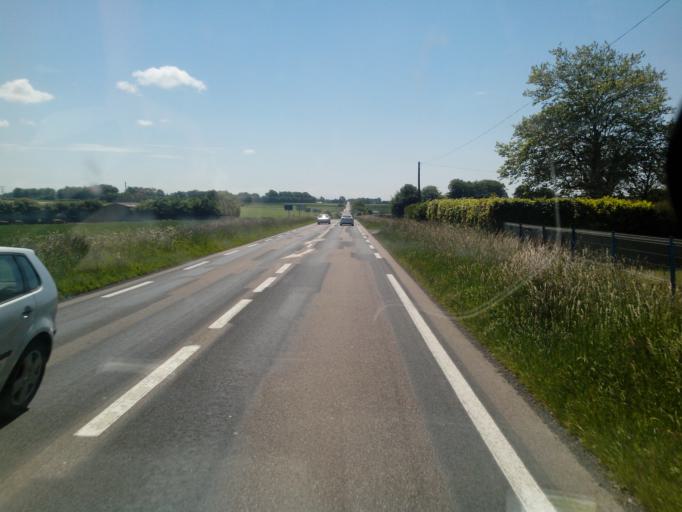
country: FR
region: Haute-Normandie
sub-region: Departement de la Seine-Maritime
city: Etainhus
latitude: 49.6100
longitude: 0.2872
